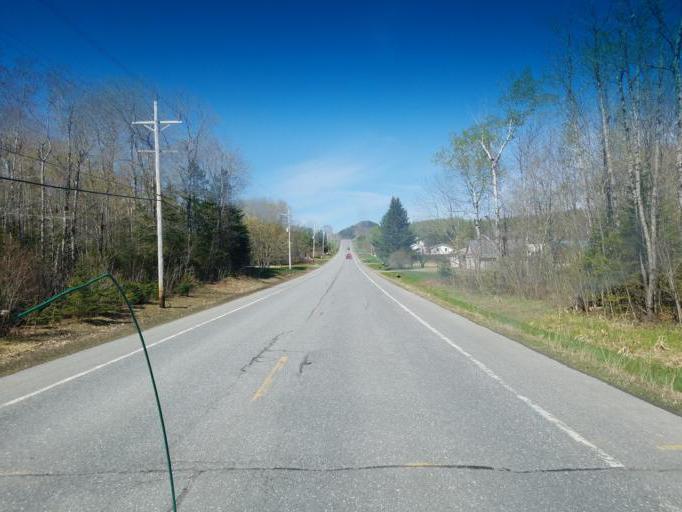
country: US
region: Maine
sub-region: Aroostook County
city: Presque Isle
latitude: 46.6668
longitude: -68.2039
